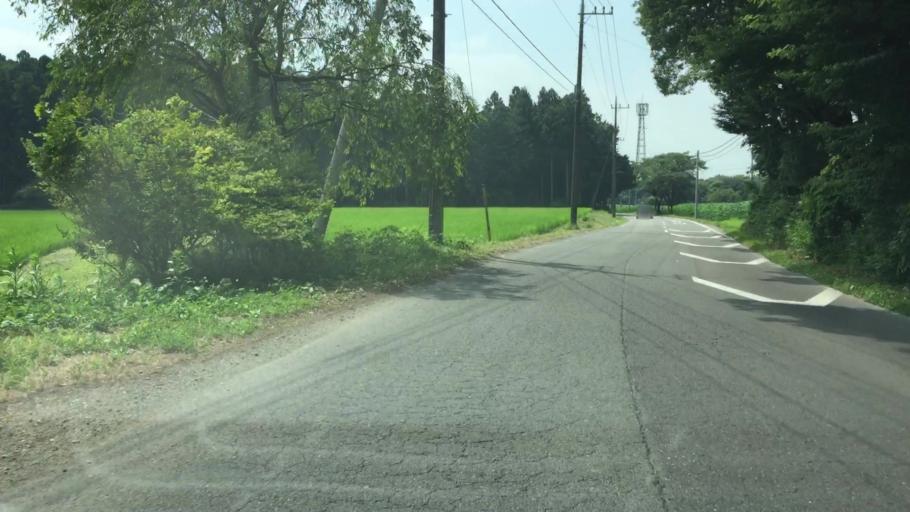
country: JP
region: Tochigi
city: Kuroiso
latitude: 36.9551
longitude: 139.9585
